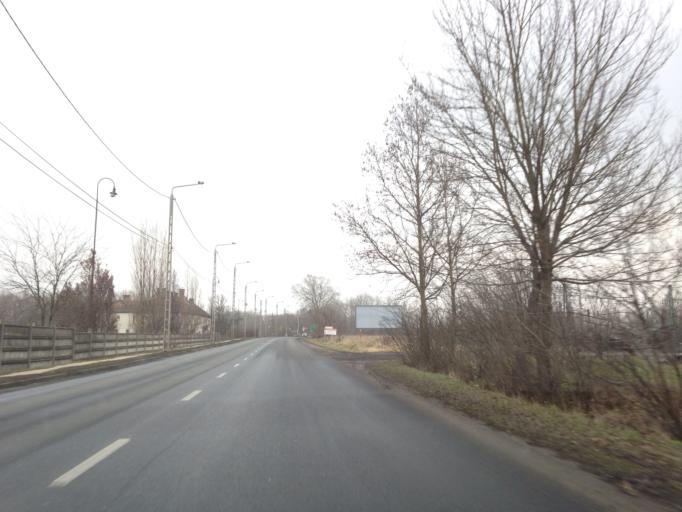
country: HU
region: Komarom-Esztergom
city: Almasfuzito
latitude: 47.7243
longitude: 18.2665
